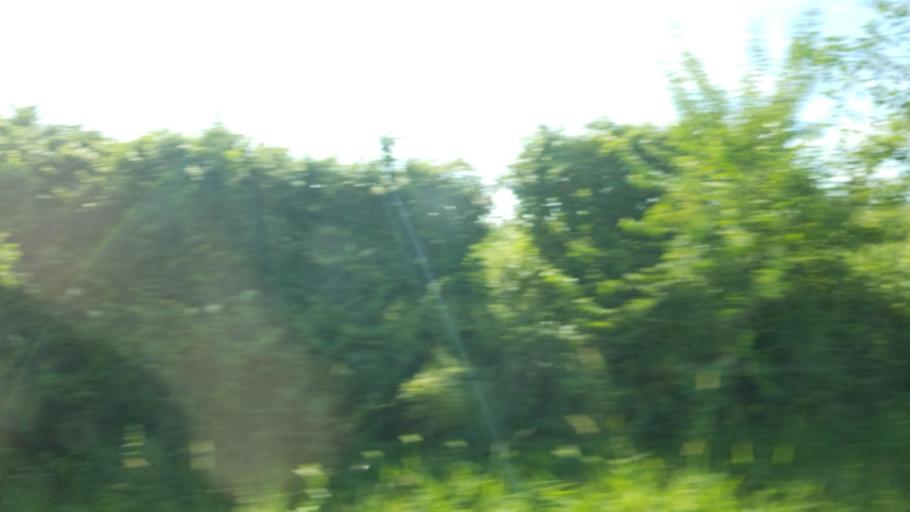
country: US
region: Illinois
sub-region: Saline County
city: Harrisburg
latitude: 37.8204
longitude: -88.5487
